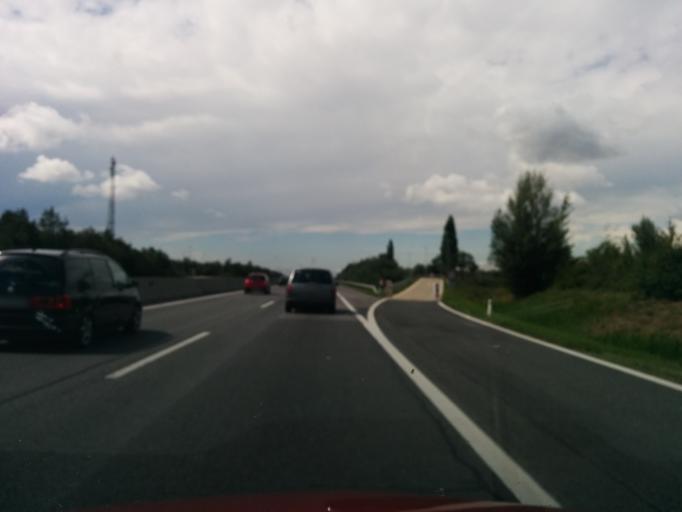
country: AT
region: Burgenland
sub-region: Politischer Bezirk Neusiedl am See
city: Zurndorf
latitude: 47.9408
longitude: 16.9613
